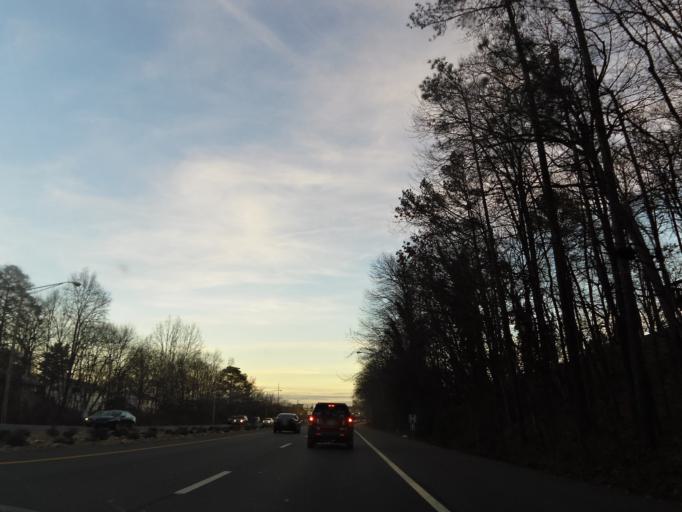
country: US
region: Tennessee
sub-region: Bradley County
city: Cleveland
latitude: 35.1879
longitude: -84.8783
